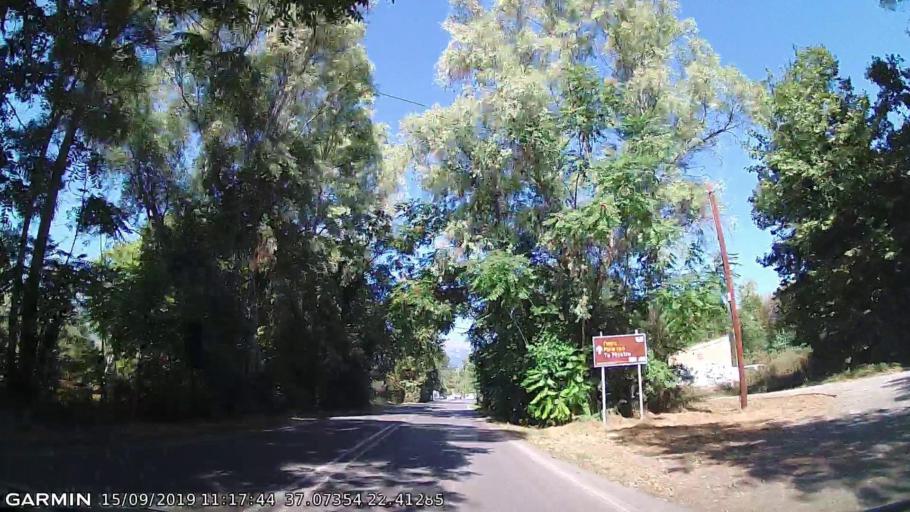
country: GR
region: Peloponnese
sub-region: Nomos Lakonias
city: Magoula
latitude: 37.0736
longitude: 22.4127
